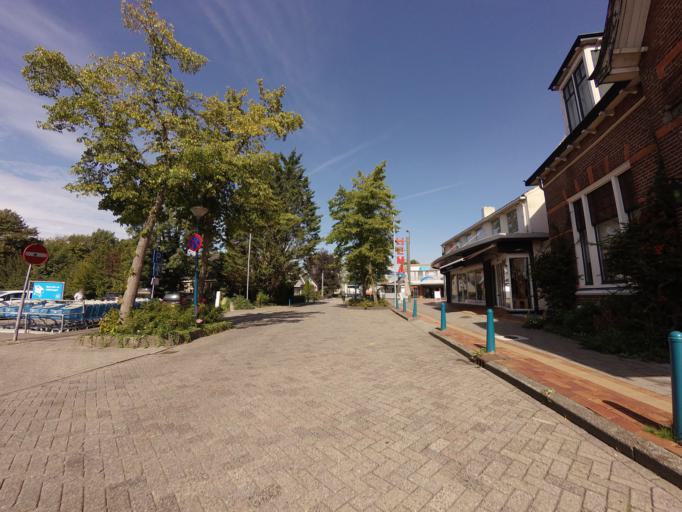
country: NL
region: Utrecht
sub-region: Gemeente De Ronde Venen
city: Mijdrecht
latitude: 52.2053
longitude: 4.8662
